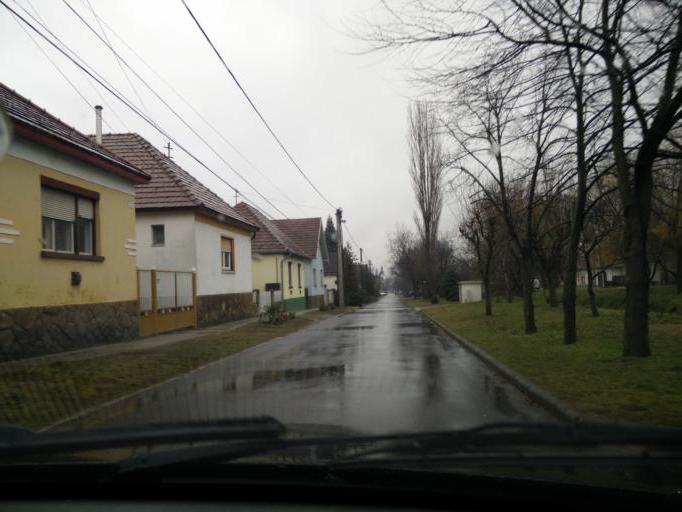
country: HU
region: Pest
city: Pilisszentivan
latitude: 47.6118
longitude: 18.8928
